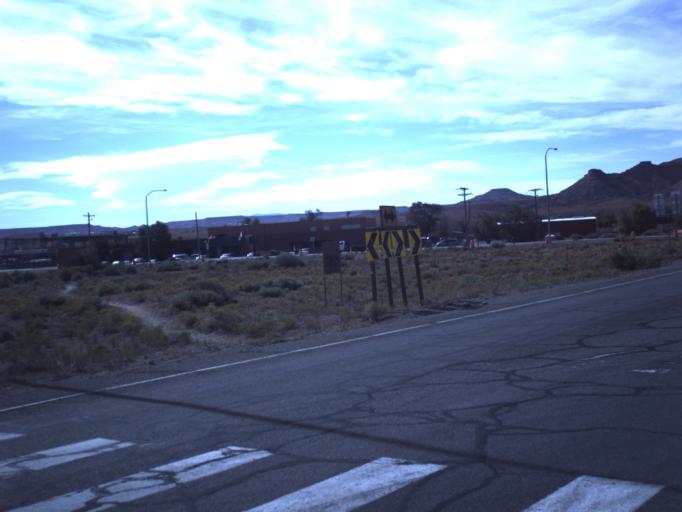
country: US
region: Utah
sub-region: San Juan County
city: Blanding
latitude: 37.2626
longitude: -109.3057
